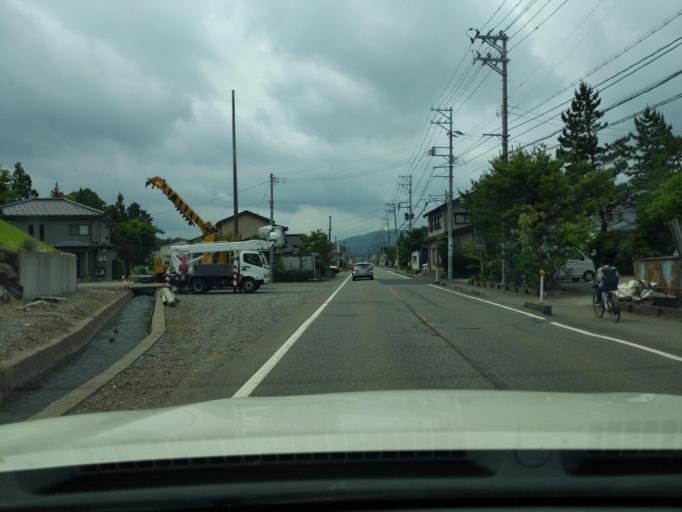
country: JP
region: Niigata
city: Kashiwazaki
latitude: 37.3492
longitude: 138.5701
